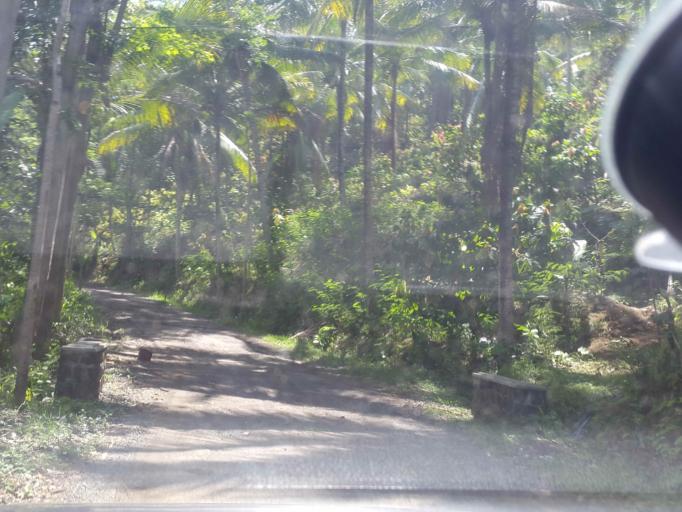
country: ID
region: East Java
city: Tawang
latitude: -8.1159
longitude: 111.6033
